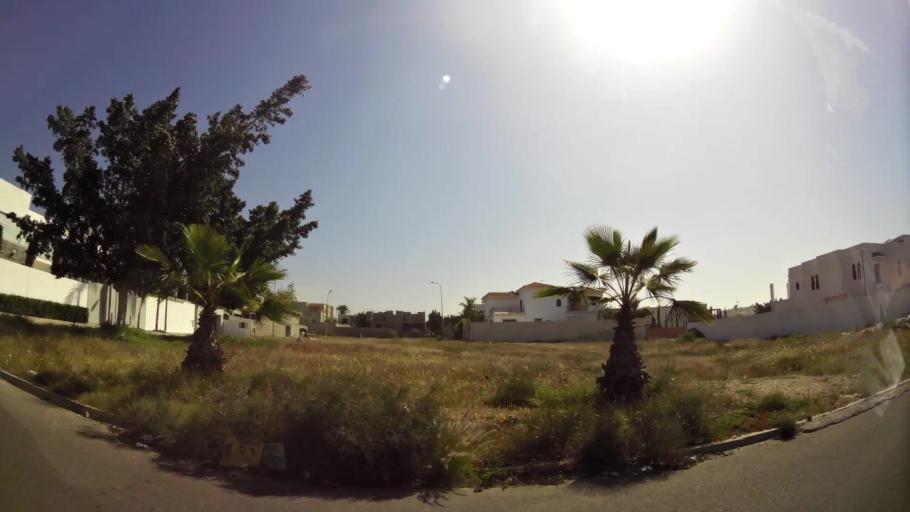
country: MA
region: Souss-Massa-Draa
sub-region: Agadir-Ida-ou-Tnan
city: Agadir
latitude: 30.4388
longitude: -9.5807
